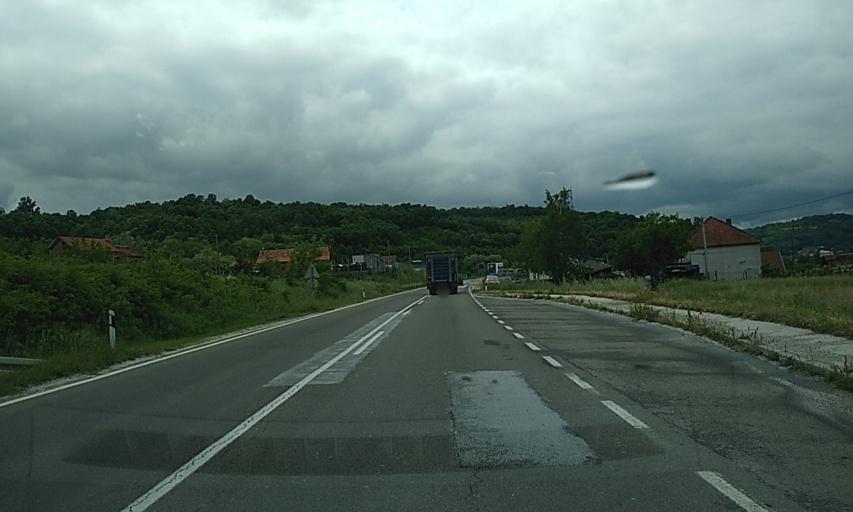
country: RS
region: Central Serbia
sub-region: Pcinjski Okrug
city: Vladicin Han
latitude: 42.7212
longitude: 22.0711
